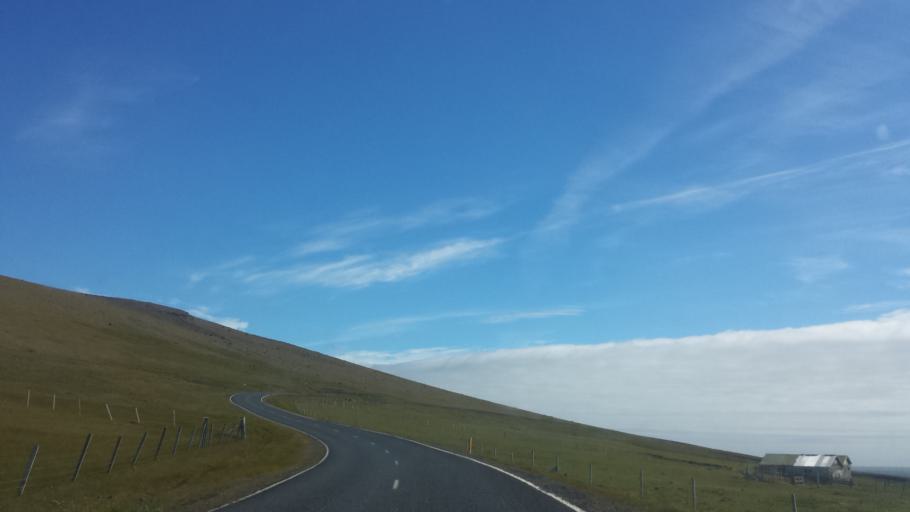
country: IS
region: South
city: Vestmannaeyjar
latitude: 63.4137
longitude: -20.2843
